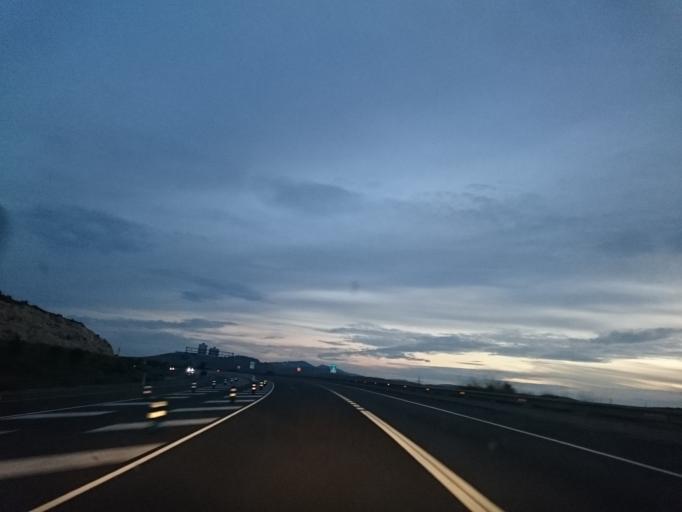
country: ES
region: Catalonia
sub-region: Provincia de Barcelona
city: Vilafranca del Penedes
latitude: 41.3292
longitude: 1.7120
